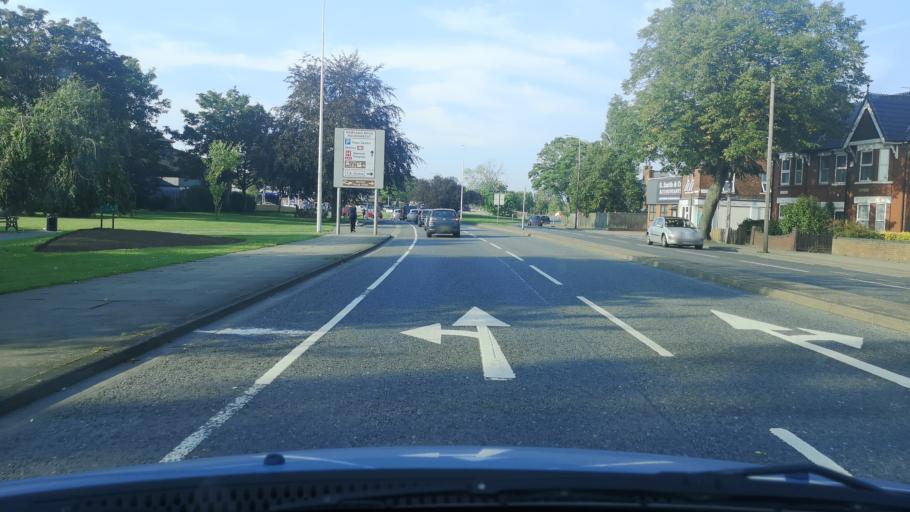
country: GB
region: England
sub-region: North Lincolnshire
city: Scunthorpe
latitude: 53.5833
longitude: -0.6535
